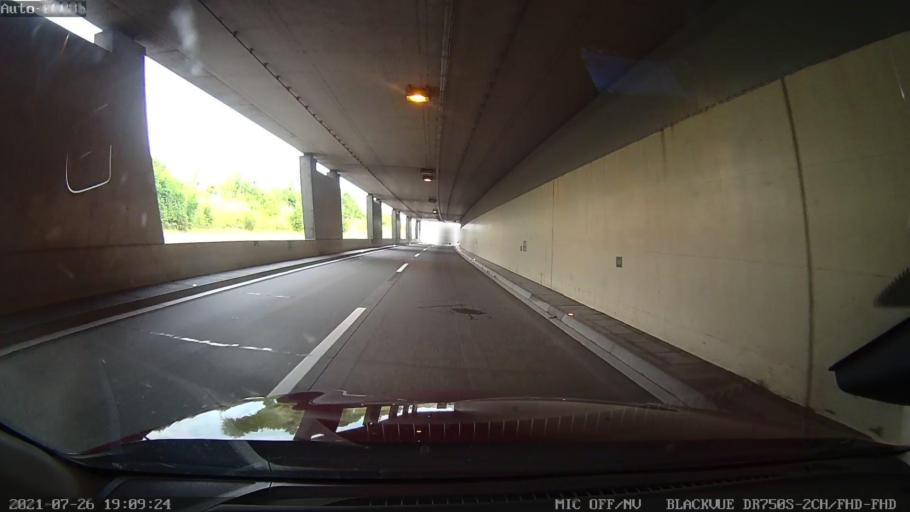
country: AT
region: Upper Austria
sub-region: Wels-Land
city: Steinhaus
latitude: 48.0984
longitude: 14.0207
